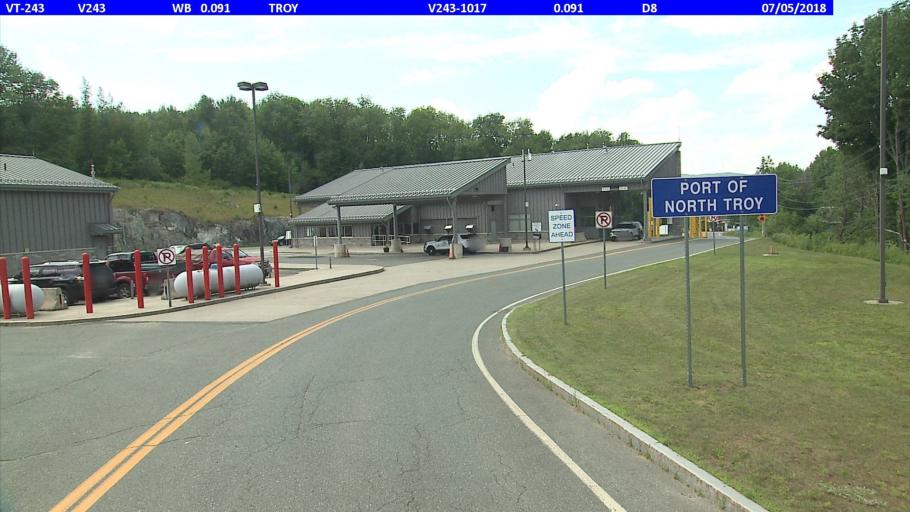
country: US
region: Vermont
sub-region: Orleans County
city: Newport
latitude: 45.0060
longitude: -72.4153
